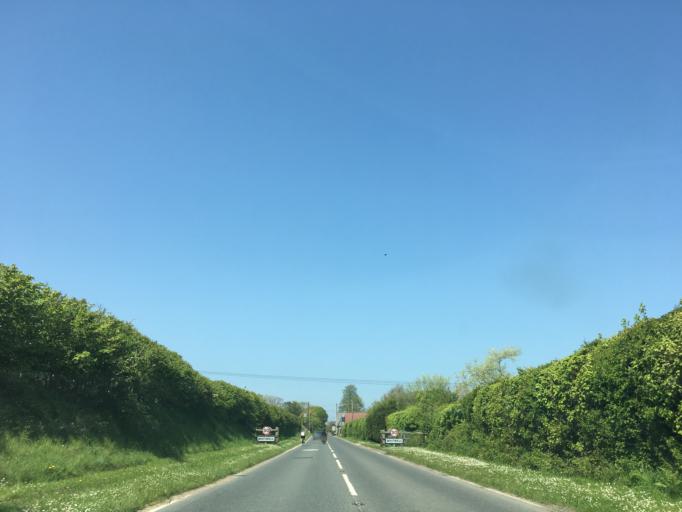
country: GB
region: England
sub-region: Isle of Wight
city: Niton
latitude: 50.5937
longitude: -1.2618
